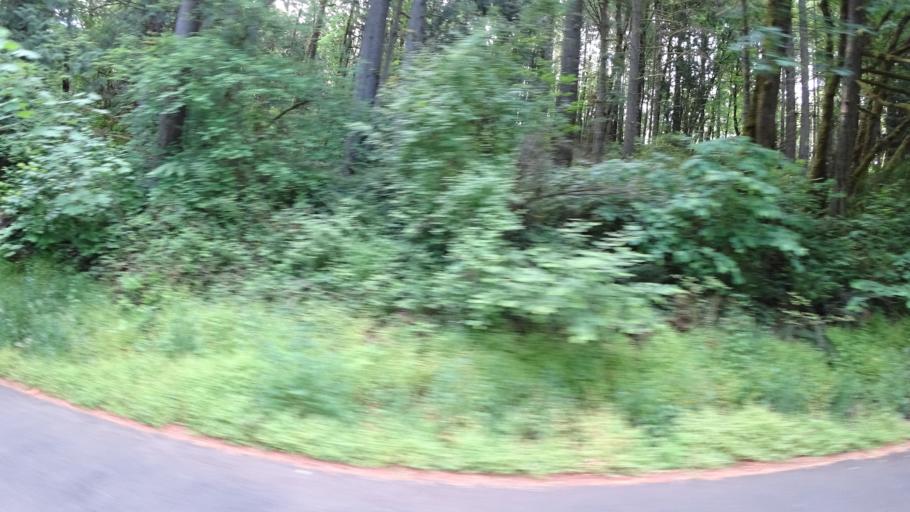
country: US
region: Oregon
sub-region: Washington County
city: Oak Hills
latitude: 45.5811
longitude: -122.8157
